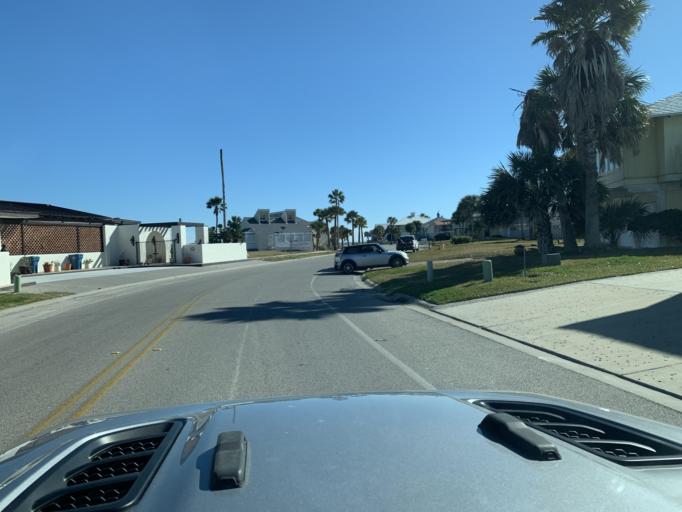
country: US
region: Texas
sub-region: Aransas County
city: Fulton
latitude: 28.0391
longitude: -97.0259
